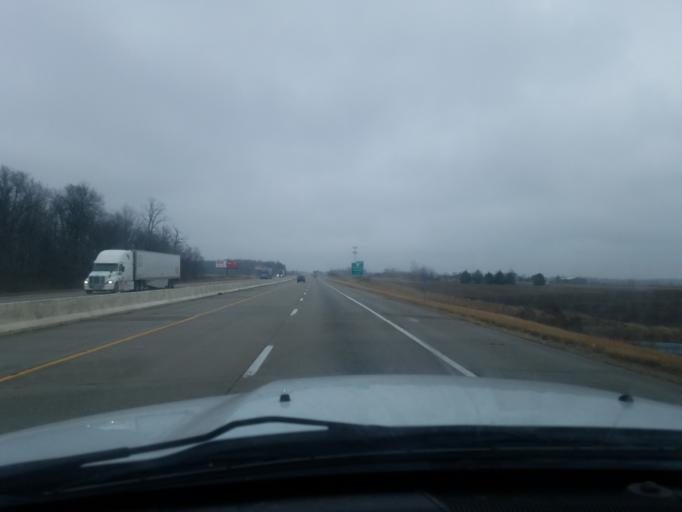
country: US
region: Indiana
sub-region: Wells County
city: Ossian
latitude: 40.9526
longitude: -85.1942
